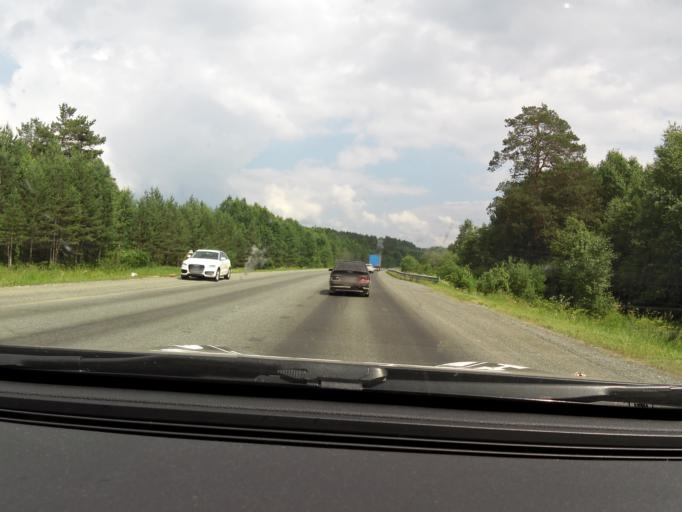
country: RU
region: Sverdlovsk
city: Ufimskiy
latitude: 56.7754
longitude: 58.2272
